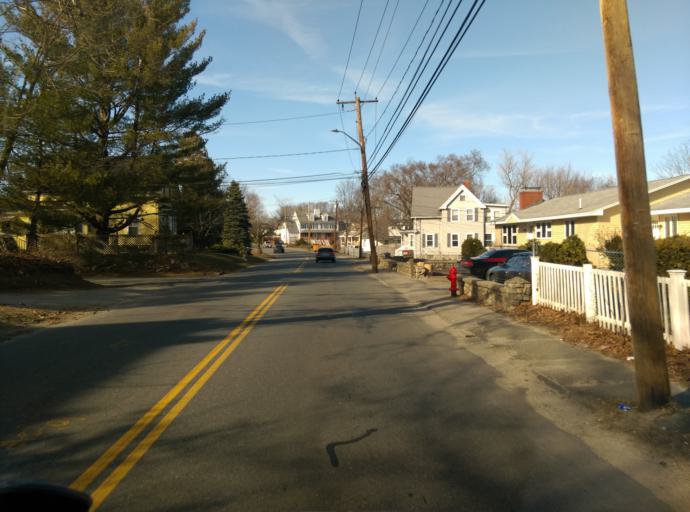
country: US
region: Massachusetts
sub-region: Essex County
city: North Andover
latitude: 42.7233
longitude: -71.1411
